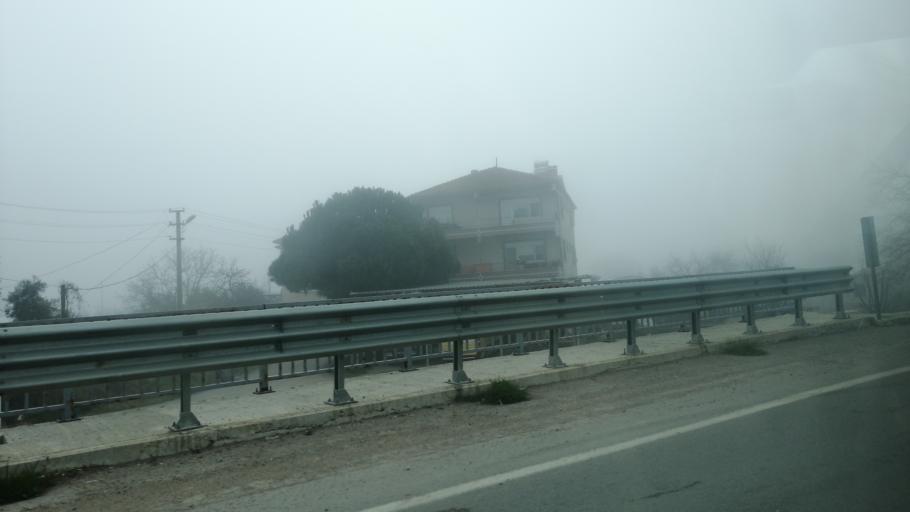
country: TR
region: Yalova
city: Korukoy
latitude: 40.6537
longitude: 29.1890
